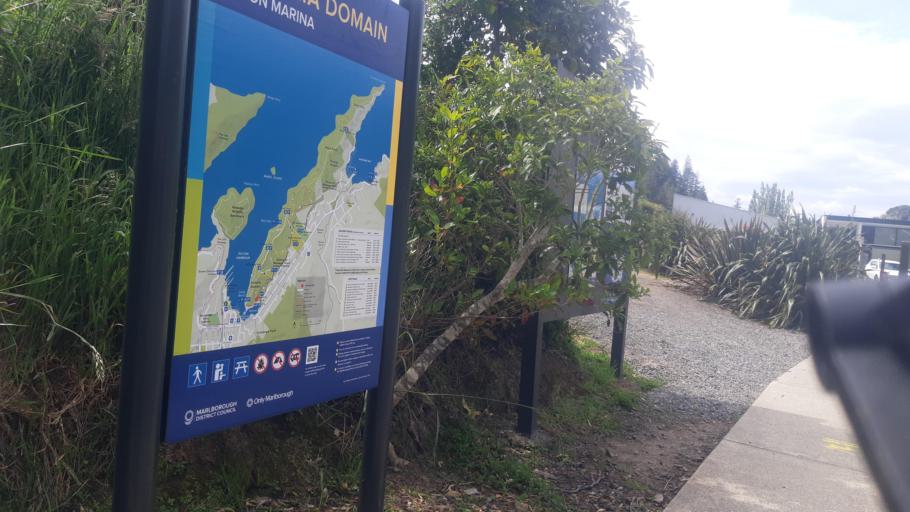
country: NZ
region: Marlborough
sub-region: Marlborough District
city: Picton
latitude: -41.2872
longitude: 174.0130
